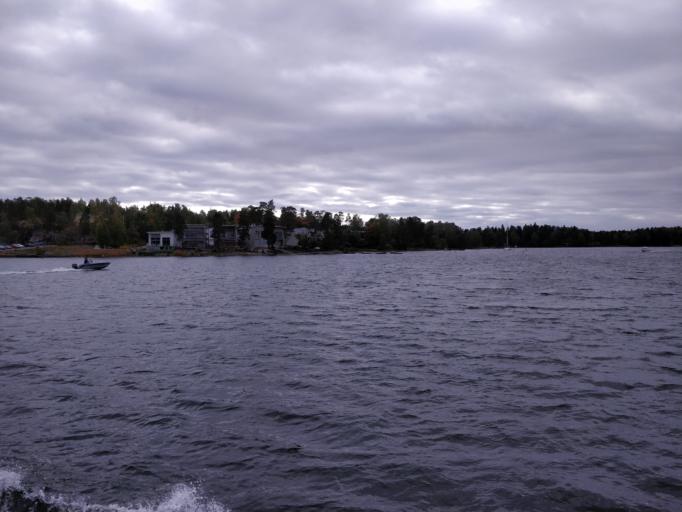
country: FI
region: Uusimaa
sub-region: Helsinki
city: Vantaa
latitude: 60.1746
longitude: 25.0817
